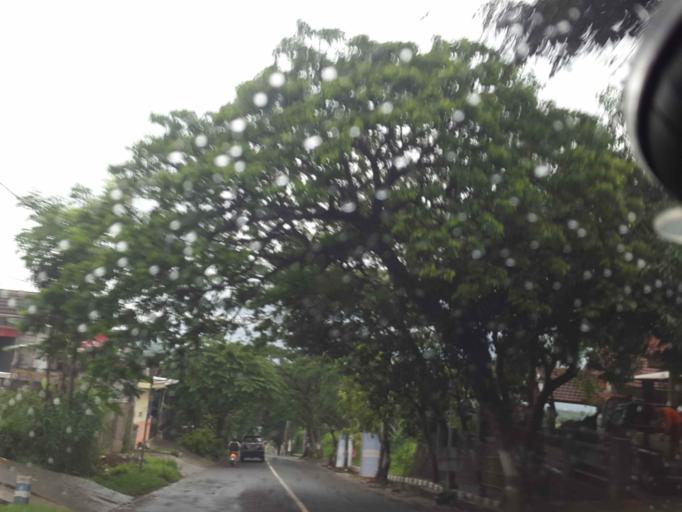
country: ID
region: East Java
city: Batu
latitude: -7.8647
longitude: 112.5452
